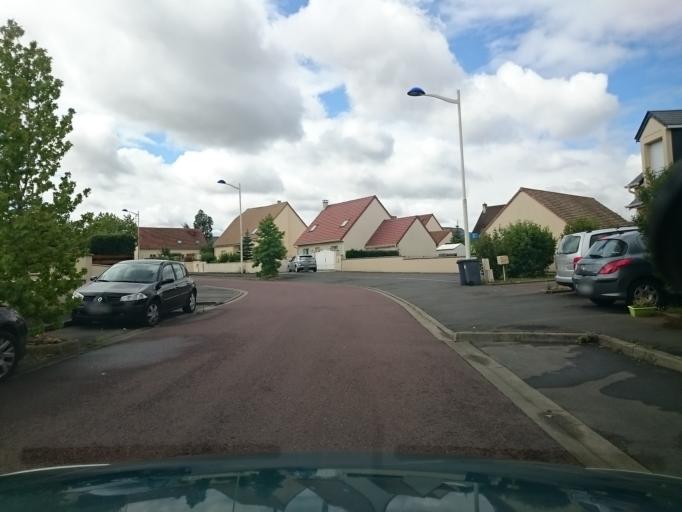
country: FR
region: Lower Normandy
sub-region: Departement du Calvados
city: Ifs
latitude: 49.1387
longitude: -0.3595
